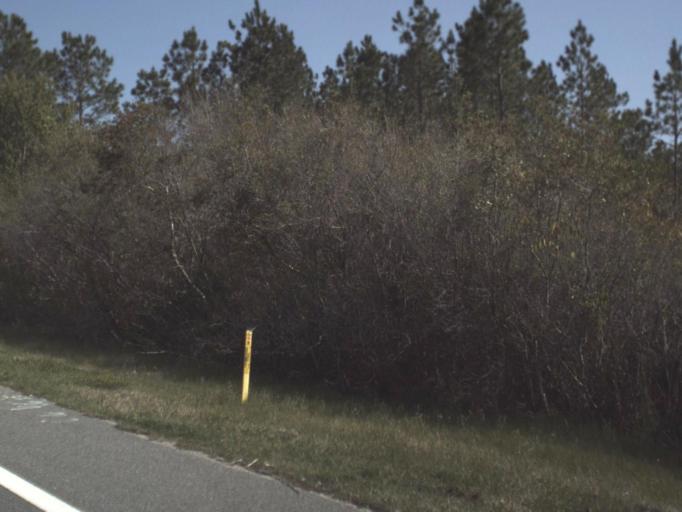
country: US
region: Florida
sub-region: Bay County
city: Lynn Haven
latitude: 30.3291
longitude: -85.7431
